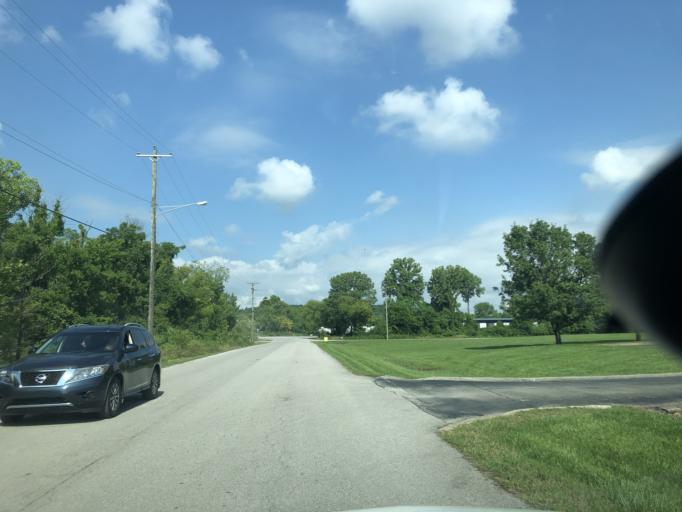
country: US
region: Tennessee
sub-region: Rutherford County
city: La Vergne
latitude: 36.0242
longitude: -86.6080
